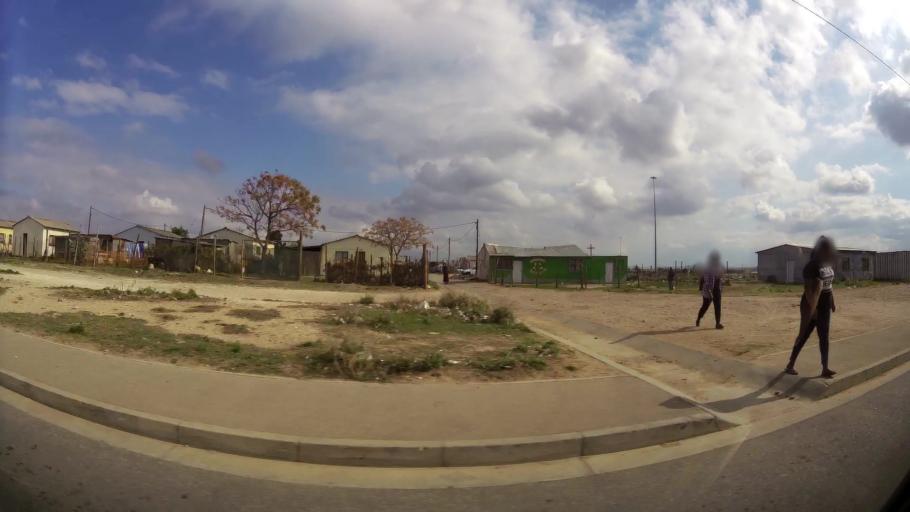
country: ZA
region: Eastern Cape
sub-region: Nelson Mandela Bay Metropolitan Municipality
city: Port Elizabeth
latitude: -33.7919
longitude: 25.5807
